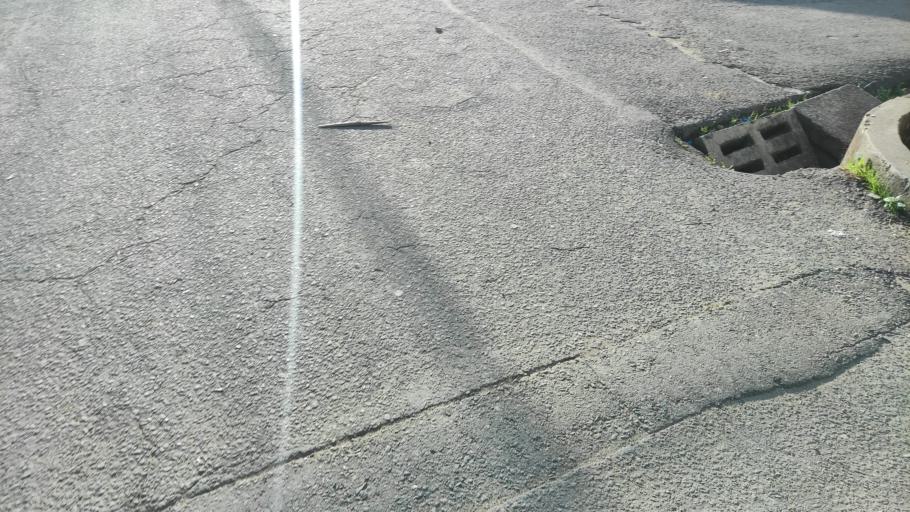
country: CO
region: Cauca
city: Popayan
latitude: 2.4893
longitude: -76.5684
